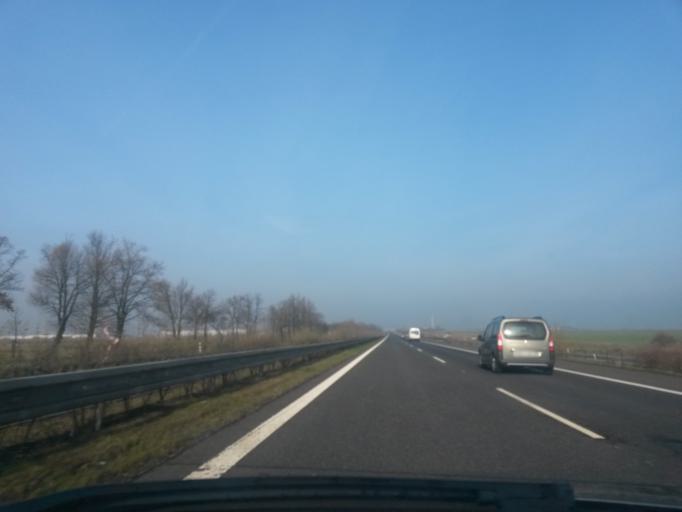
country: CZ
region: Ustecky
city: Zatec
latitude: 50.3758
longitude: 13.5962
